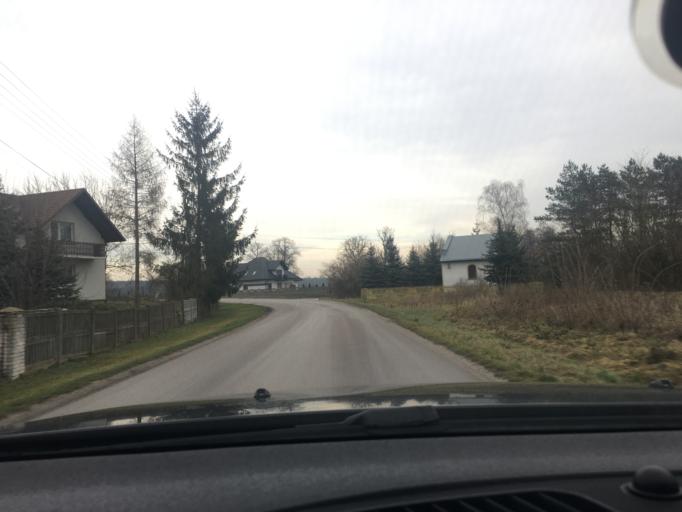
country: PL
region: Swietokrzyskie
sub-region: Powiat jedrzejowski
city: Imielno
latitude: 50.6357
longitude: 20.4125
